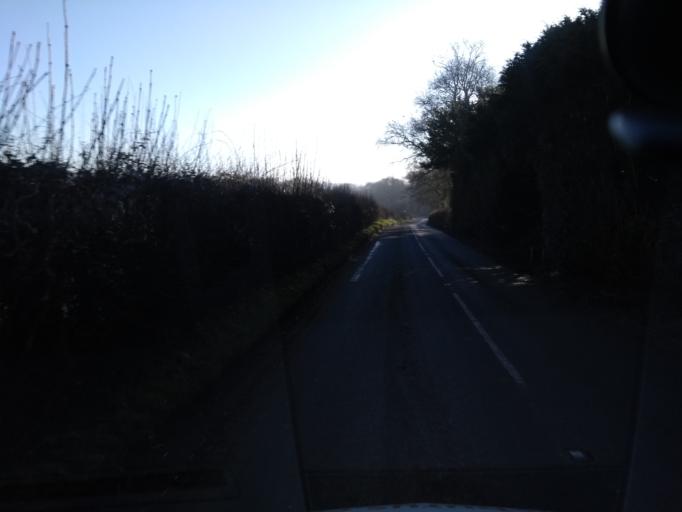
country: GB
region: England
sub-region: Somerset
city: Redlynch
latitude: 51.0855
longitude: -2.4040
